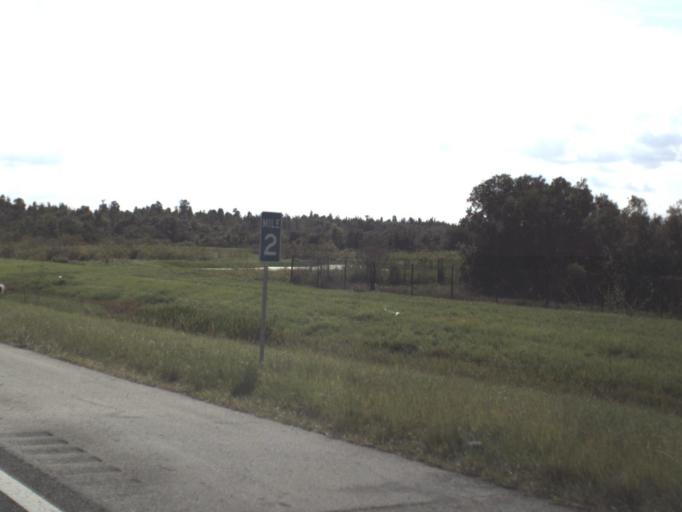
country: US
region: Florida
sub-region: Polk County
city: Winston
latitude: 28.0124
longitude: -82.0292
